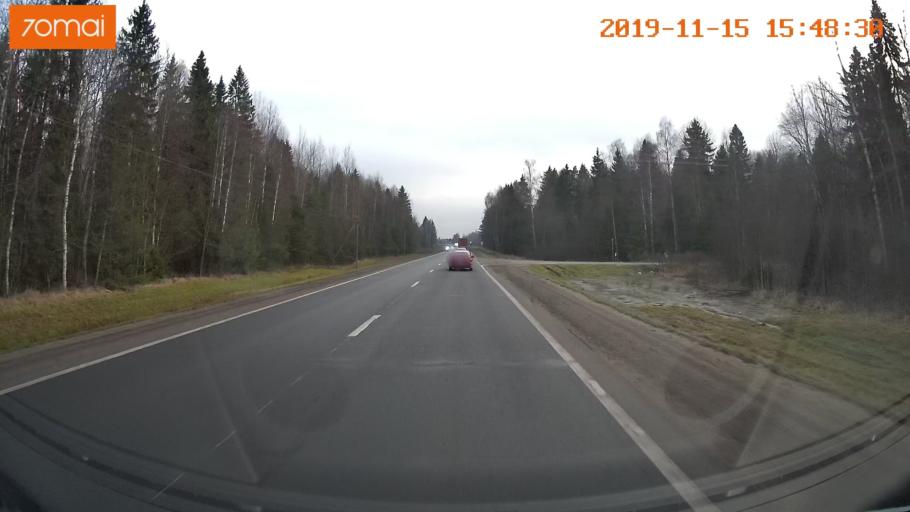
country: RU
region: Jaroslavl
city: Danilov
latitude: 57.9264
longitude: 40.0065
